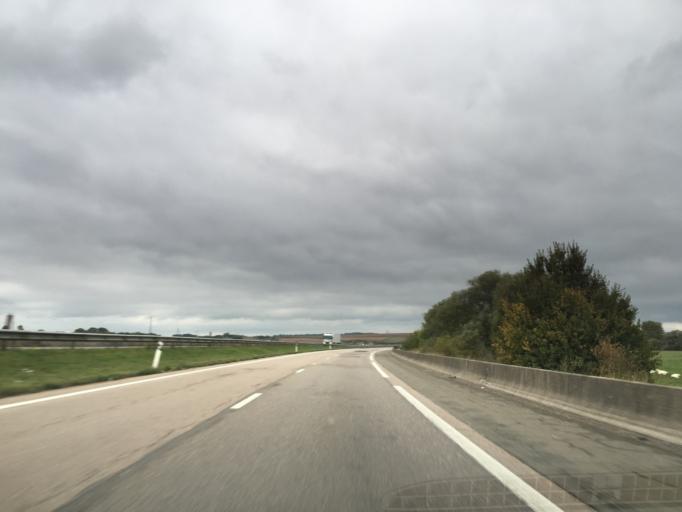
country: FR
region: Lorraine
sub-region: Departement de Meurthe-et-Moselle
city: Foug
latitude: 48.6853
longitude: 5.7136
